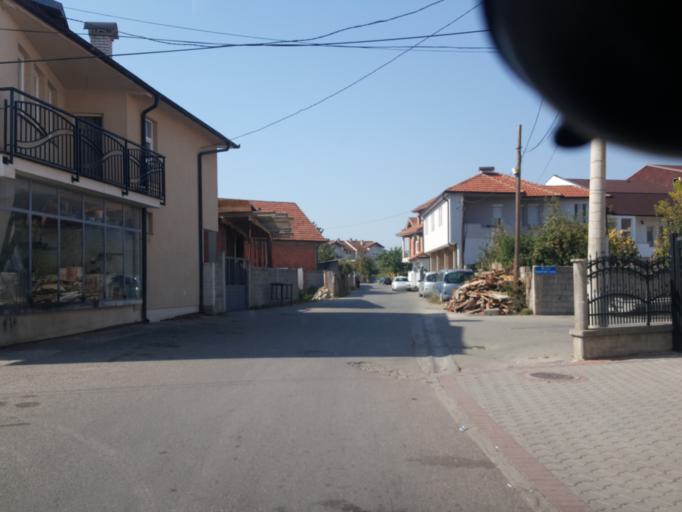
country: XK
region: Gjakova
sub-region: Komuna e Gjakoves
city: Gjakove
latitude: 42.3900
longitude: 20.4317
